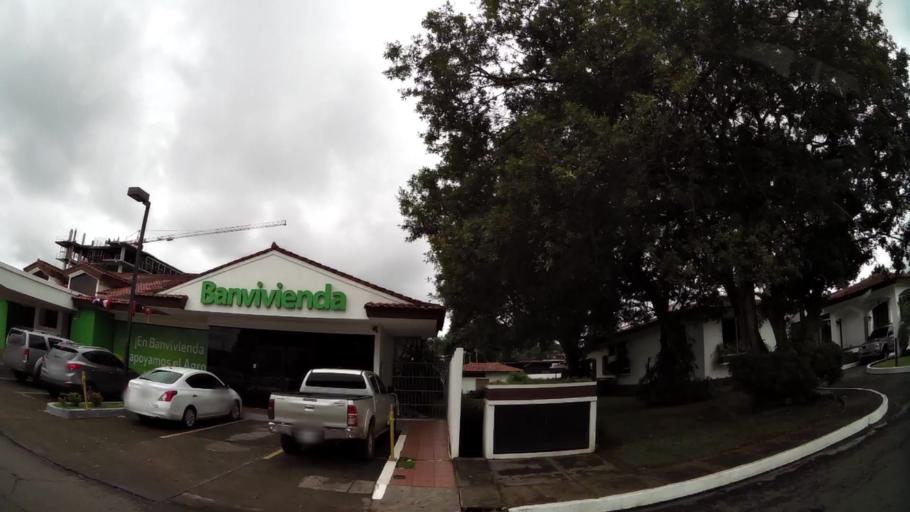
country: PA
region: Chiriqui
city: David
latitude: 8.4326
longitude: -82.4265
